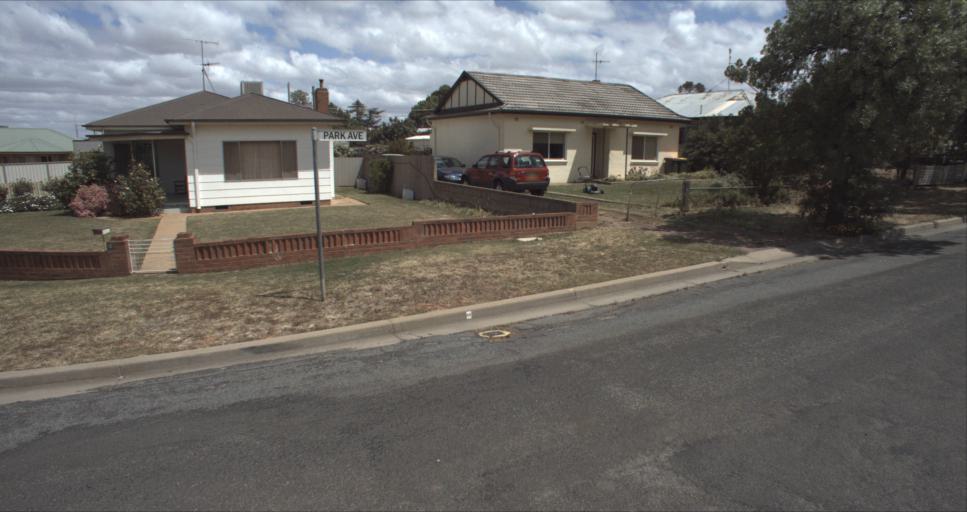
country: AU
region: New South Wales
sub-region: Leeton
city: Leeton
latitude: -34.5629
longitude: 146.3972
